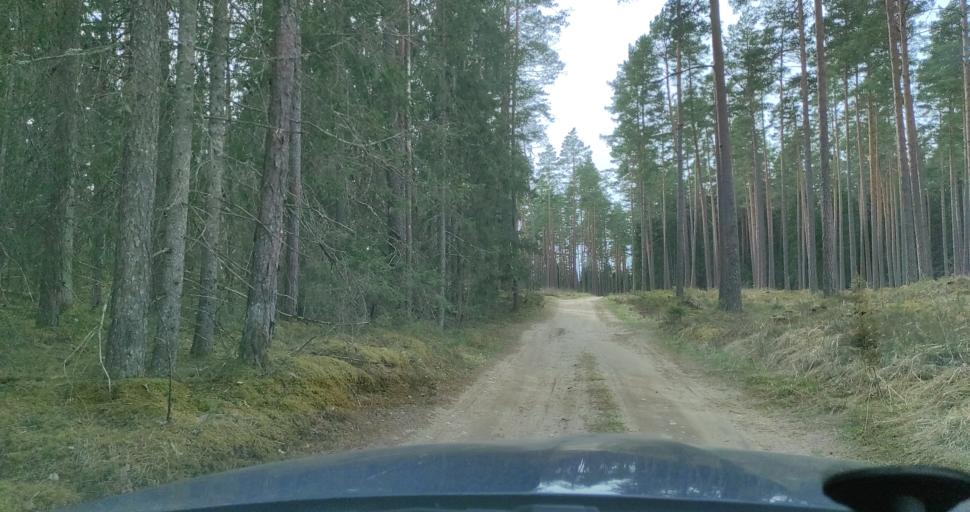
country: LV
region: Talsu Rajons
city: Stende
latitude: 57.0885
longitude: 22.3994
